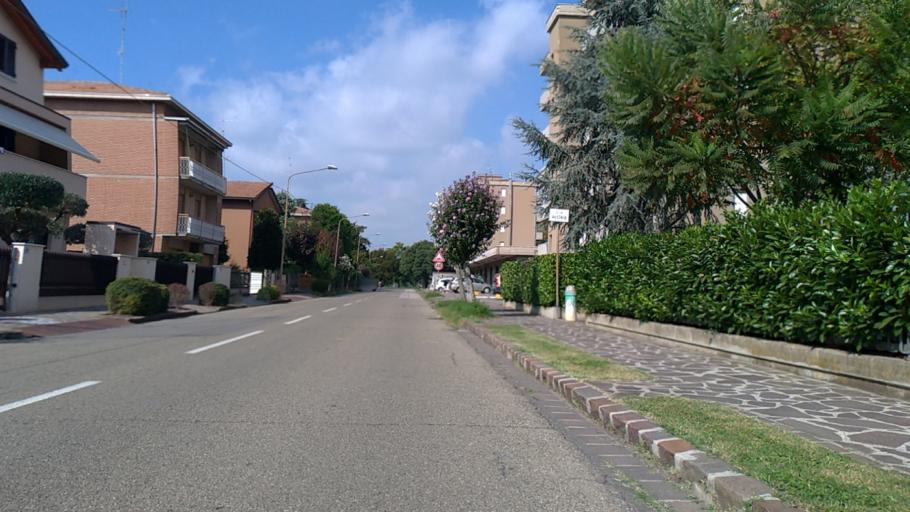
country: IT
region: Emilia-Romagna
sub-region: Provincia di Modena
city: Carpi Centro
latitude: 44.7692
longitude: 10.8736
